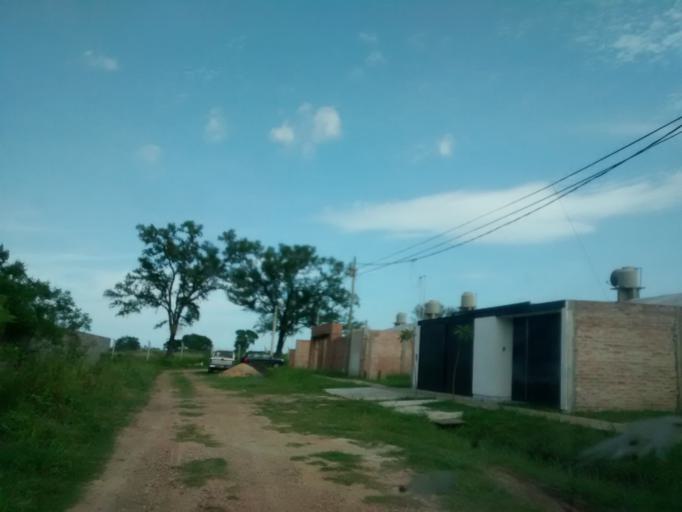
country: AR
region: Chaco
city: Resistencia
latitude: -27.4115
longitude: -58.9717
